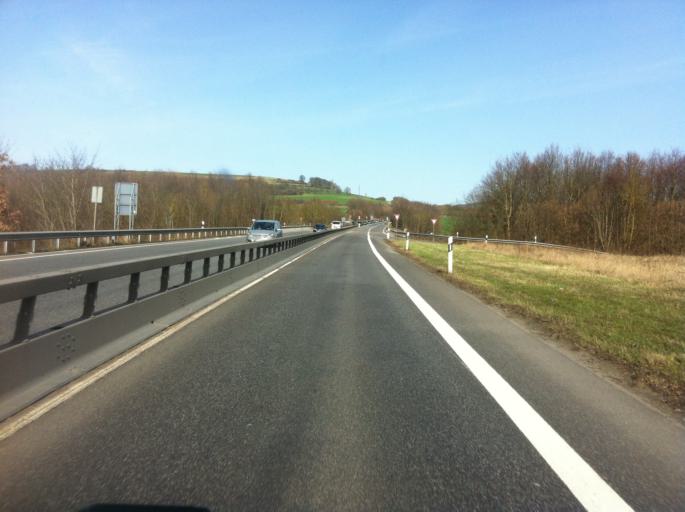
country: DE
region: Rheinland-Pfalz
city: Kottenheim
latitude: 50.3468
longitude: 7.2663
